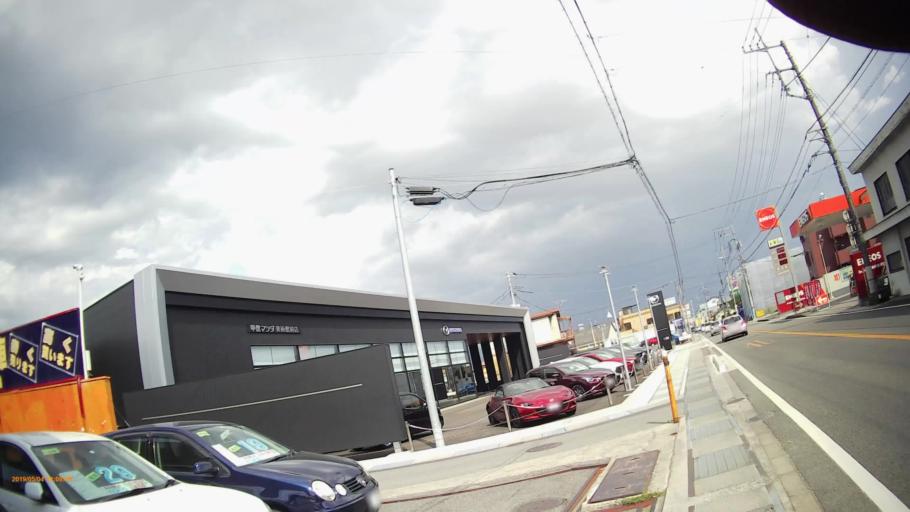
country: JP
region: Yamanashi
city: Kofu-shi
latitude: 35.6609
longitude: 138.5408
